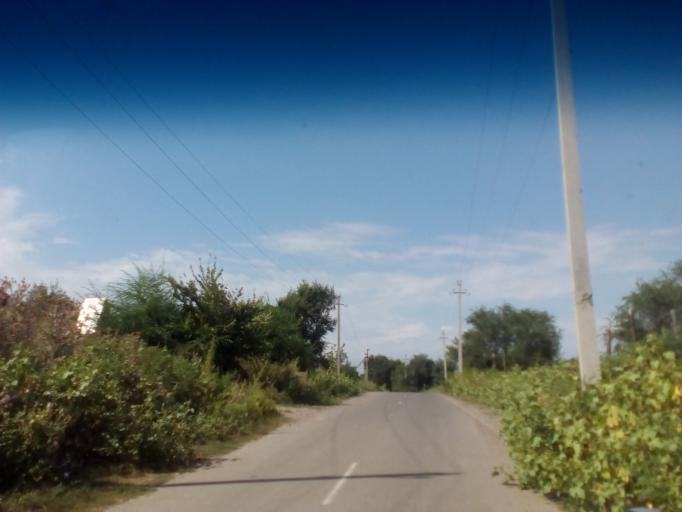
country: KZ
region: Almaty Oblysy
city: Burunday
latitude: 43.1540
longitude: 76.3832
